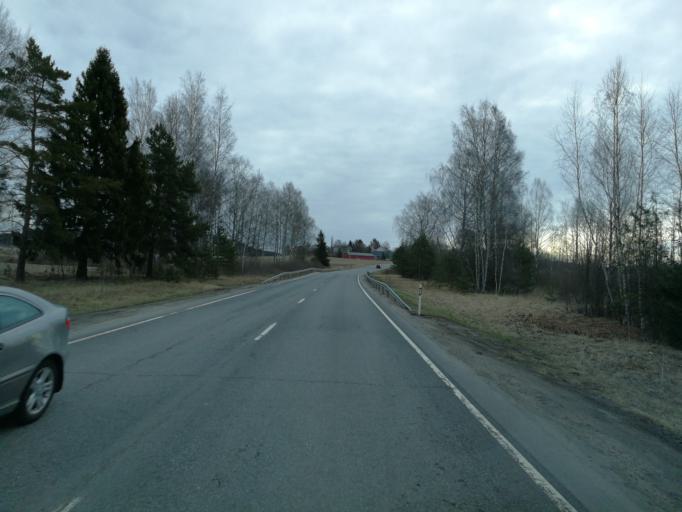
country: FI
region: Varsinais-Suomi
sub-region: Salo
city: Muurla
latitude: 60.3835
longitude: 23.2757
